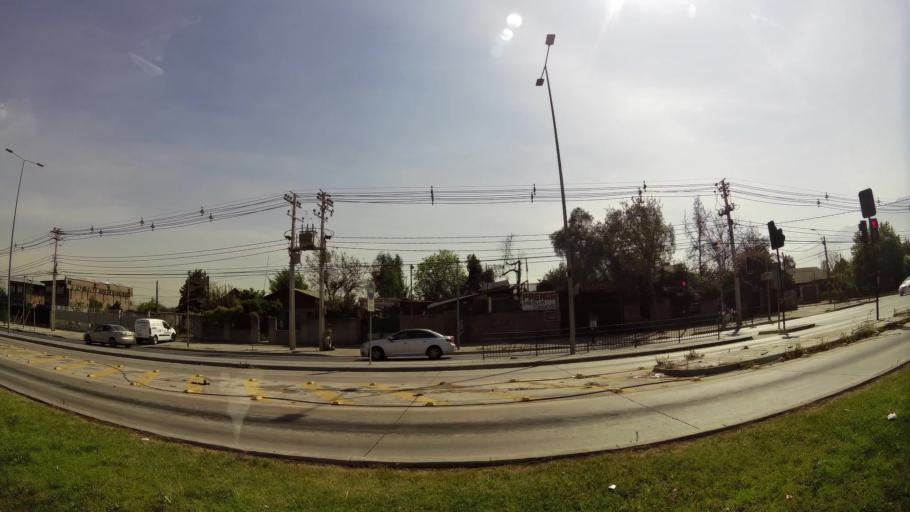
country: CL
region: Santiago Metropolitan
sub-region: Provincia de Santiago
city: Villa Presidente Frei, Nunoa, Santiago, Chile
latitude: -33.5105
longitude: -70.5805
